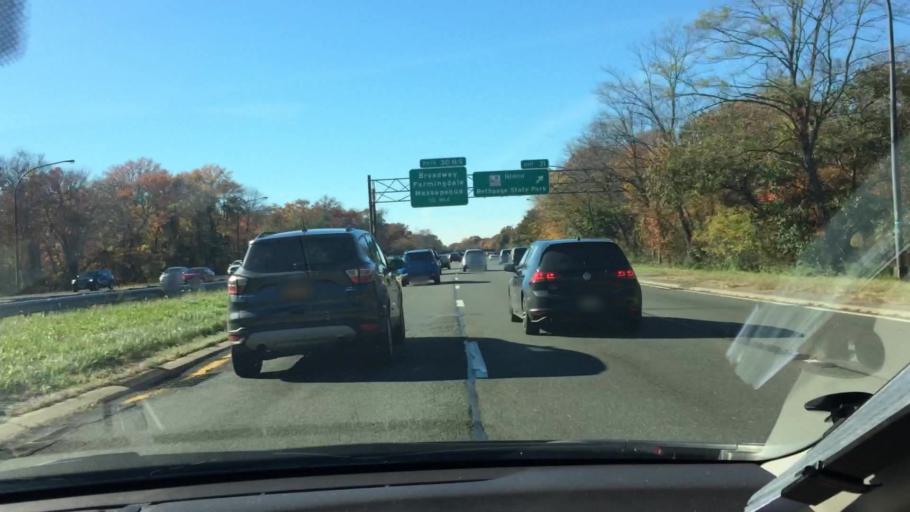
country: US
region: New York
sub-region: Nassau County
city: South Farmingdale
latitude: 40.7054
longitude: -73.4451
